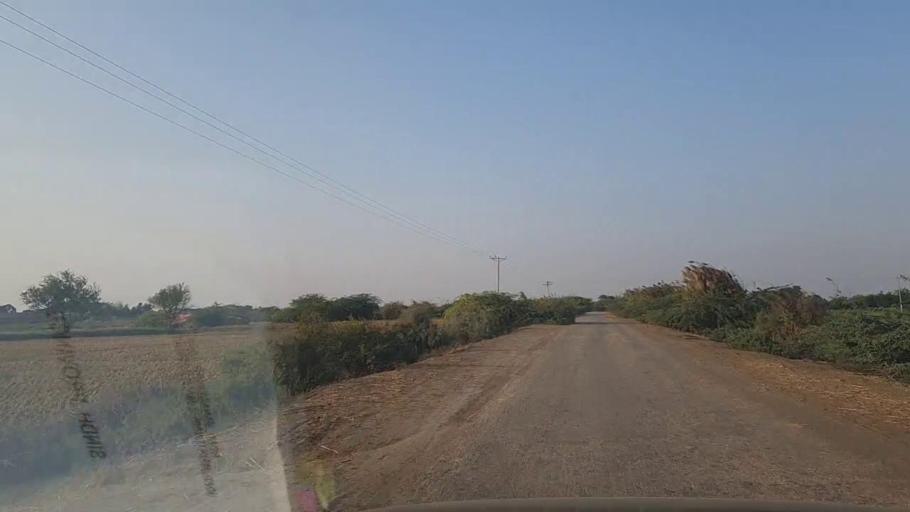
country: PK
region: Sindh
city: Keti Bandar
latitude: 24.2842
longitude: 67.5876
